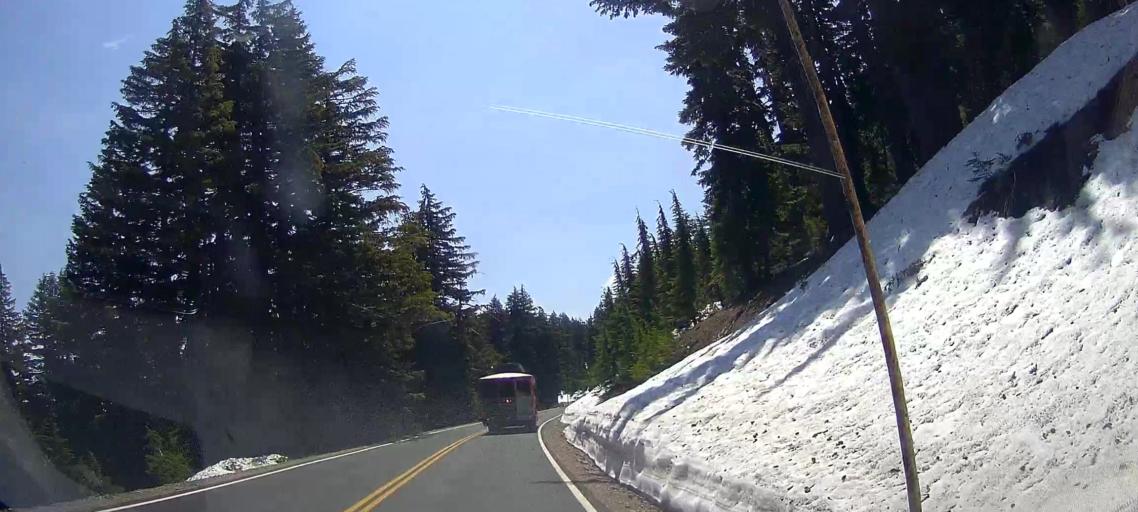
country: US
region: Oregon
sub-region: Jackson County
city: Shady Cove
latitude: 42.9819
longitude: -122.1307
